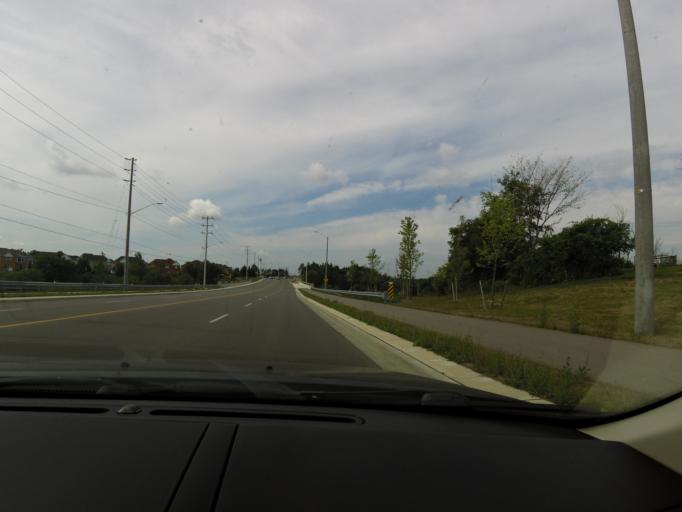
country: CA
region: Ontario
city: Brampton
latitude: 43.7858
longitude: -79.7460
